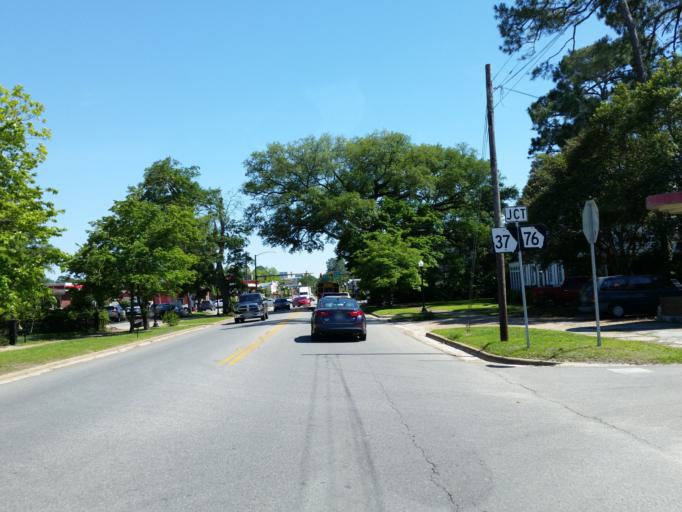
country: US
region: Georgia
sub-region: Cook County
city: Adel
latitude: 31.1383
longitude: -83.4239
